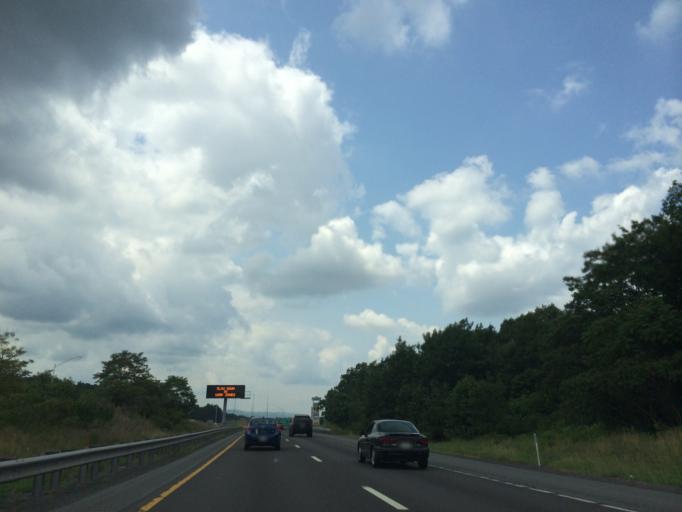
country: US
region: Pennsylvania
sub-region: Luzerne County
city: Hudson
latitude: 41.2403
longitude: -75.8345
